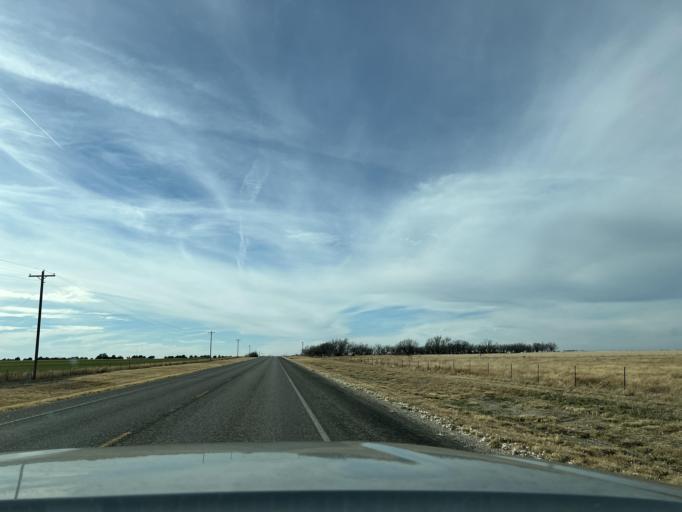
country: US
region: Texas
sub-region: Jones County
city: Anson
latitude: 32.7513
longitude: -99.8596
